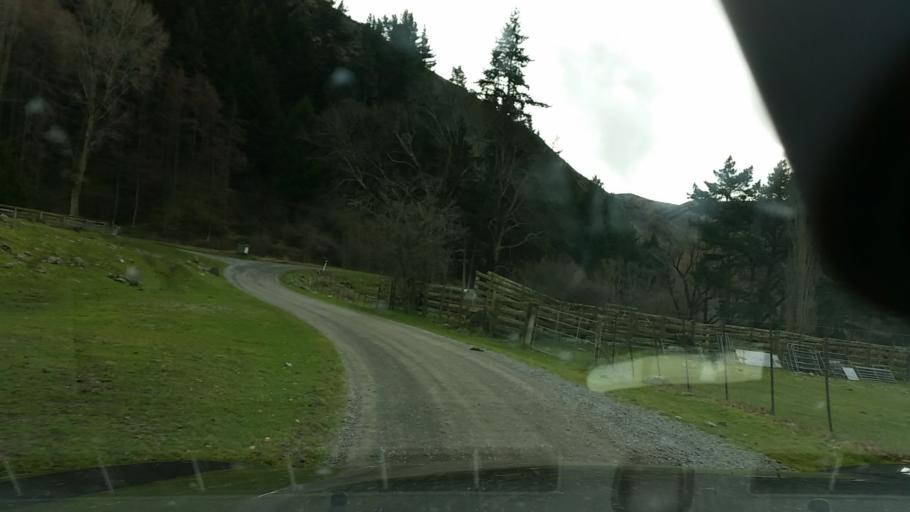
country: NZ
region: Tasman
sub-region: Tasman District
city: Richmond
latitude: -41.7272
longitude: 173.4702
